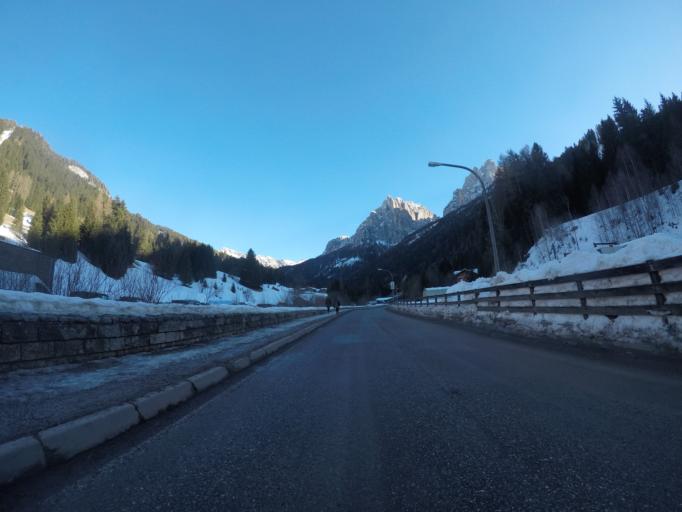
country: IT
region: Trentino-Alto Adige
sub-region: Provincia di Trento
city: Pozza di Fassa
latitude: 46.4274
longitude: 11.6979
